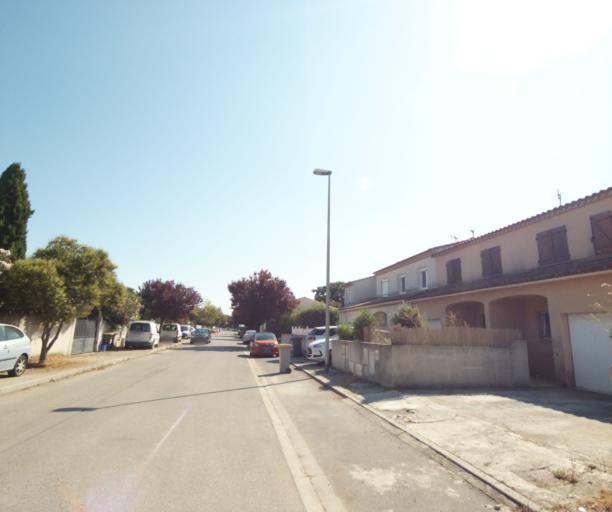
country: FR
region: Languedoc-Roussillon
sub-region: Departement de l'Herault
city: Marsillargues
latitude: 43.6679
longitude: 4.1682
